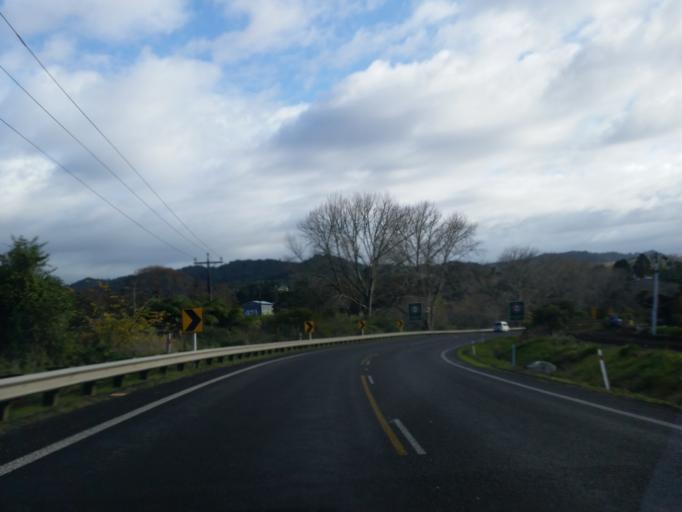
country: NZ
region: Waikato
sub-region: Hauraki District
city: Waihi
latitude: -37.4152
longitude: 175.7798
